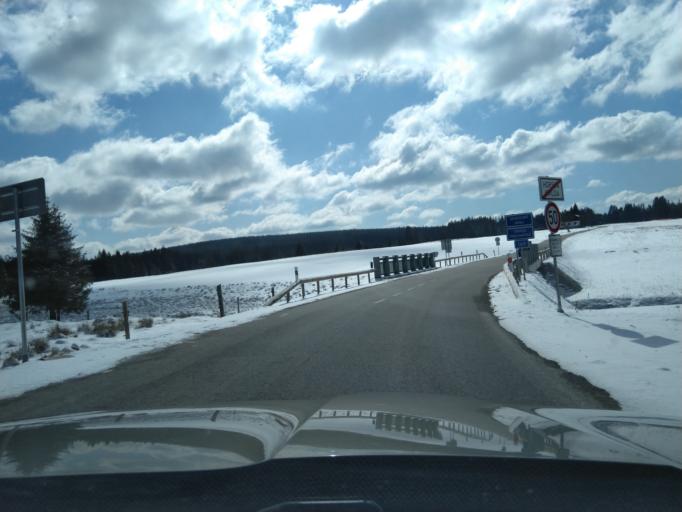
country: CZ
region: Plzensky
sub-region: Okres Klatovy
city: Kasperske Hory
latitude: 49.0487
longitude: 13.5773
